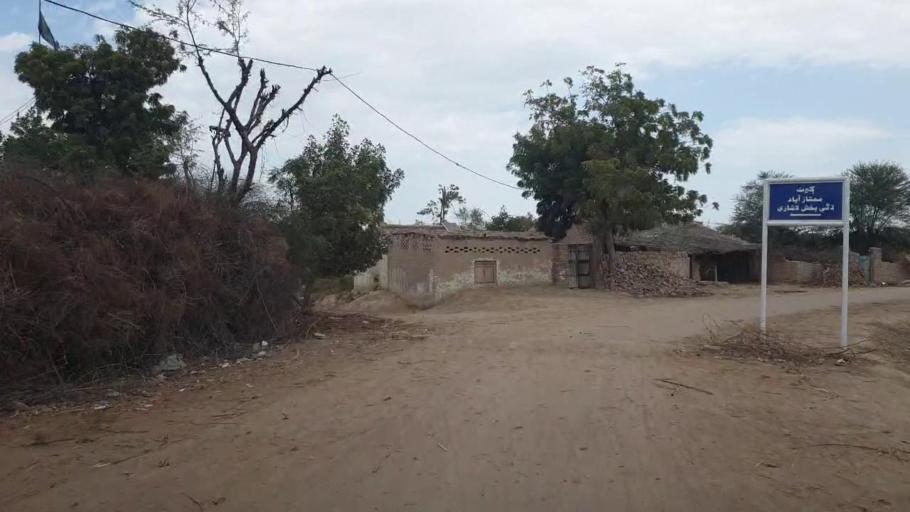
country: PK
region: Sindh
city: Hala
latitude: 25.9793
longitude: 68.4062
